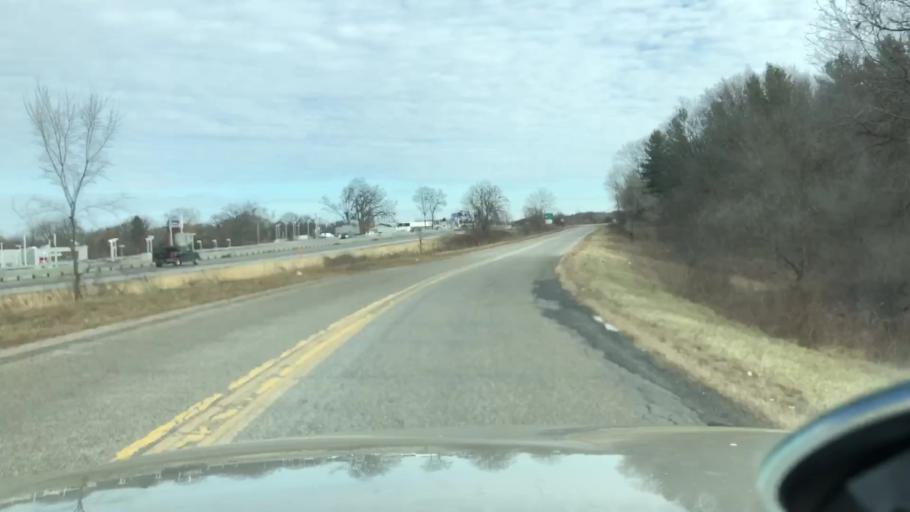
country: US
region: Michigan
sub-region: Jackson County
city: Jackson
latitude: 42.2756
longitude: -84.3787
